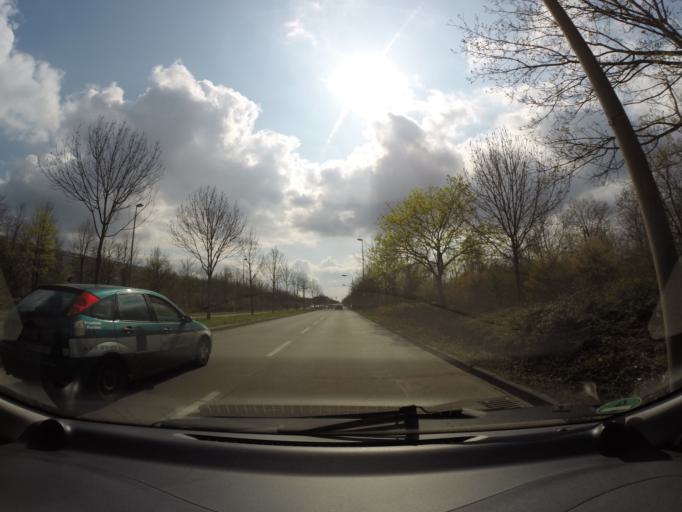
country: DE
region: Berlin
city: Kaulsdorf
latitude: 52.5334
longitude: 13.5891
